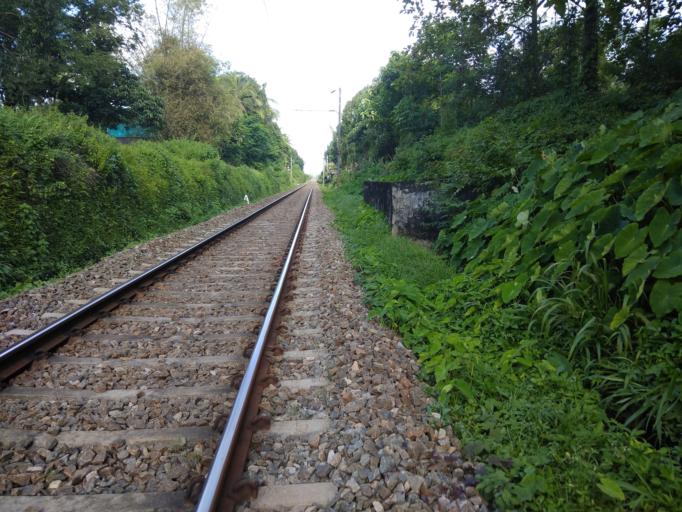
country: IN
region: Kerala
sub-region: Thrissur District
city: Avanoor
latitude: 10.5609
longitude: 76.1754
